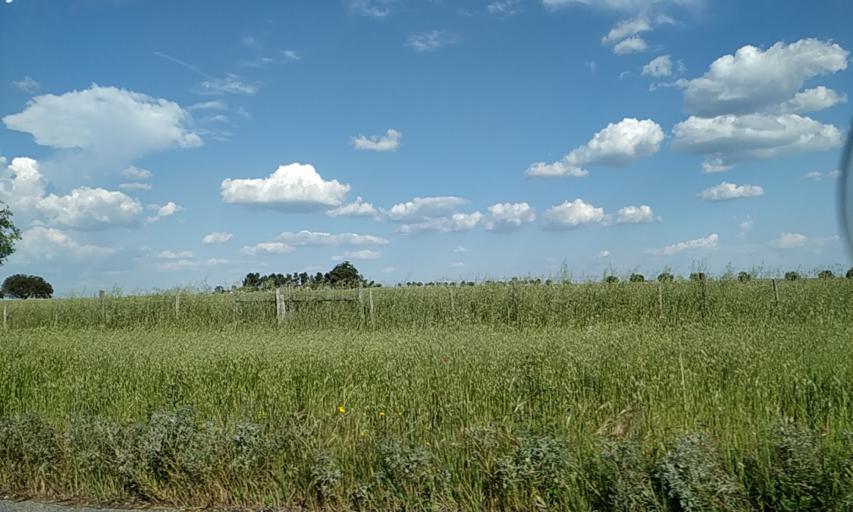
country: PT
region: Evora
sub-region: Estremoz
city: Estremoz
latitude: 38.9837
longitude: -7.4816
